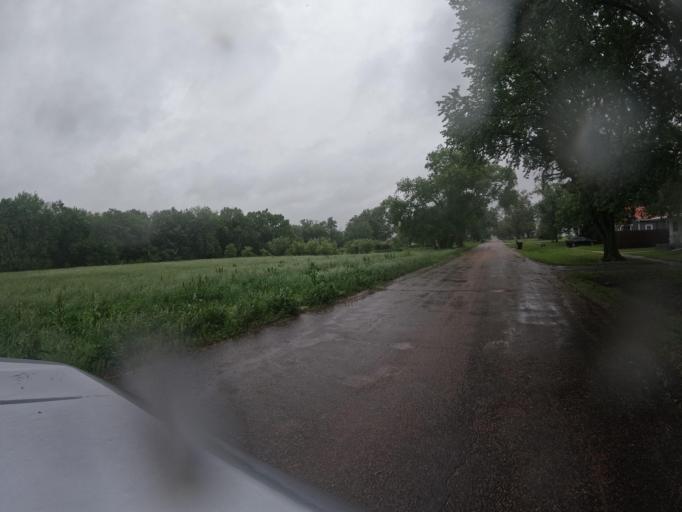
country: US
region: Nebraska
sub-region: Gage County
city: Wymore
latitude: 40.1242
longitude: -96.6593
